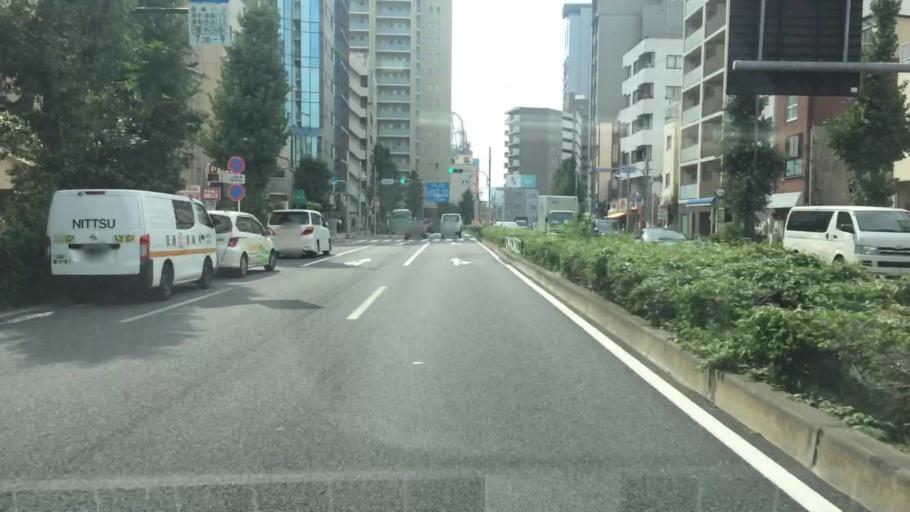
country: JP
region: Tokyo
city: Tokyo
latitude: 35.7073
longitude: 139.7580
